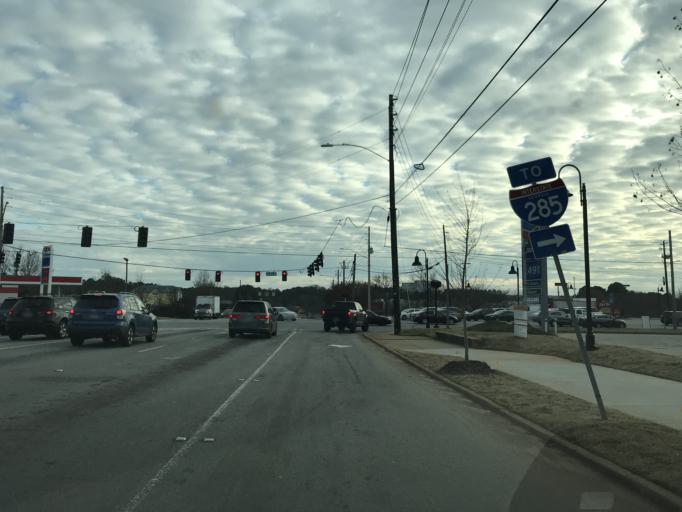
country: US
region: Georgia
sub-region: DeKalb County
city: Tucker
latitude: 33.8474
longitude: -84.2448
